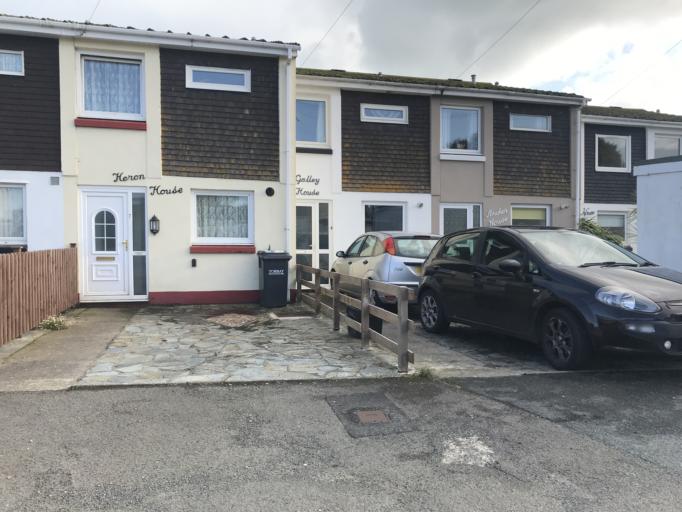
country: GB
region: England
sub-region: Borough of Torbay
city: Brixham
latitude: 50.3973
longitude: -3.5148
